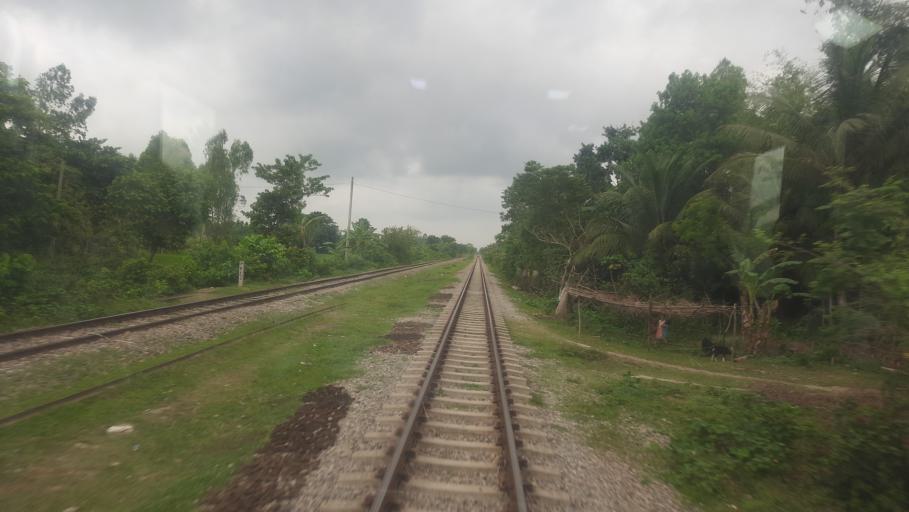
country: BD
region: Dhaka
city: Bhairab Bazar
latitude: 24.0012
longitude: 90.8897
